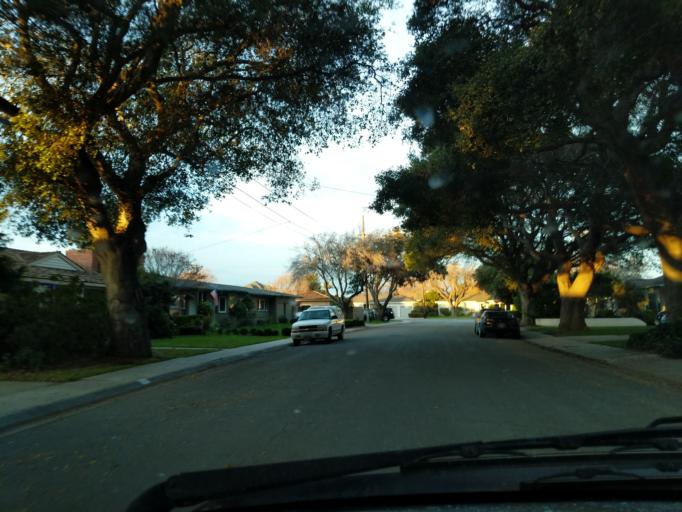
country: US
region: California
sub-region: Monterey County
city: Salinas
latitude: 36.6654
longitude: -121.6614
